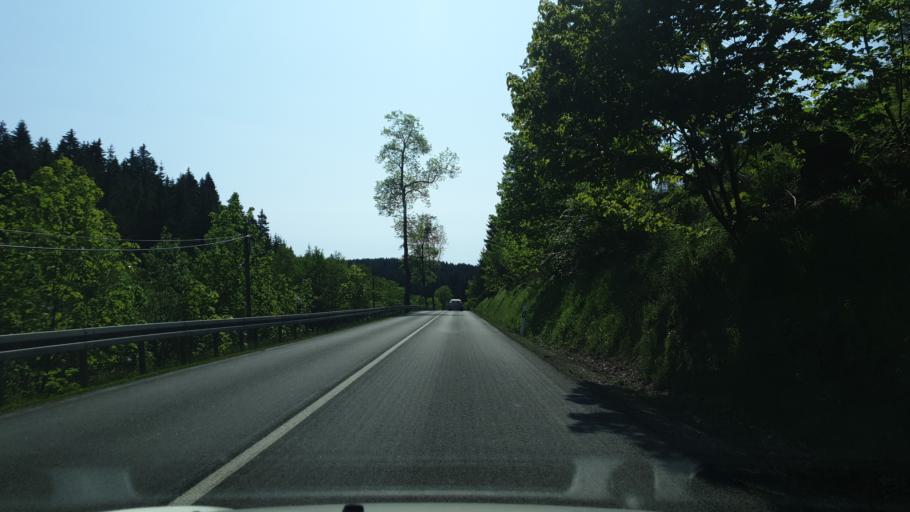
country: DE
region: Saxony
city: Tannenbergsthal
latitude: 50.4187
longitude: 12.4764
